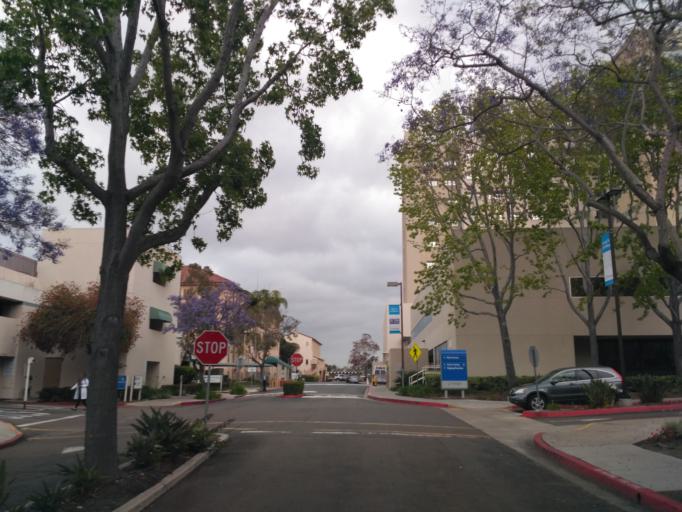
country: US
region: California
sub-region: San Diego County
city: San Diego
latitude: 32.7518
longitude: -117.1611
